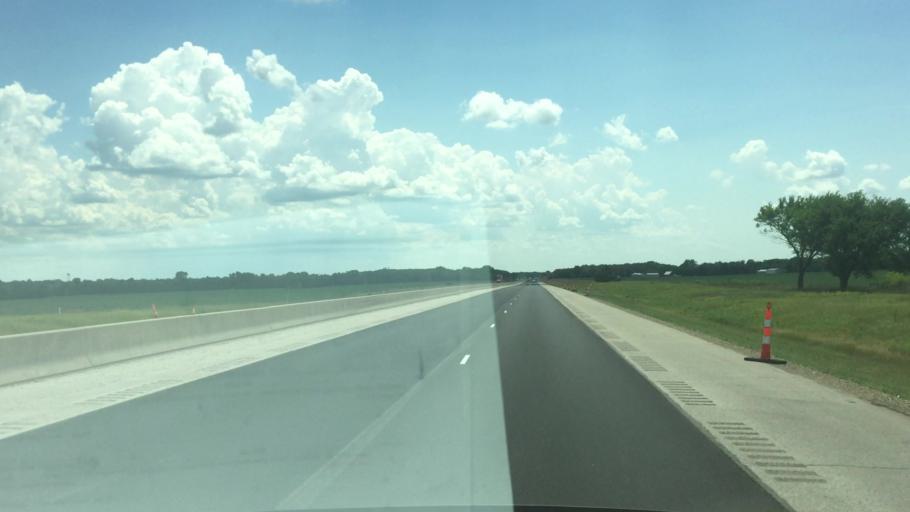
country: US
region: Kansas
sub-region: Lyon County
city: Emporia
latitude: 38.5312
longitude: -96.1368
